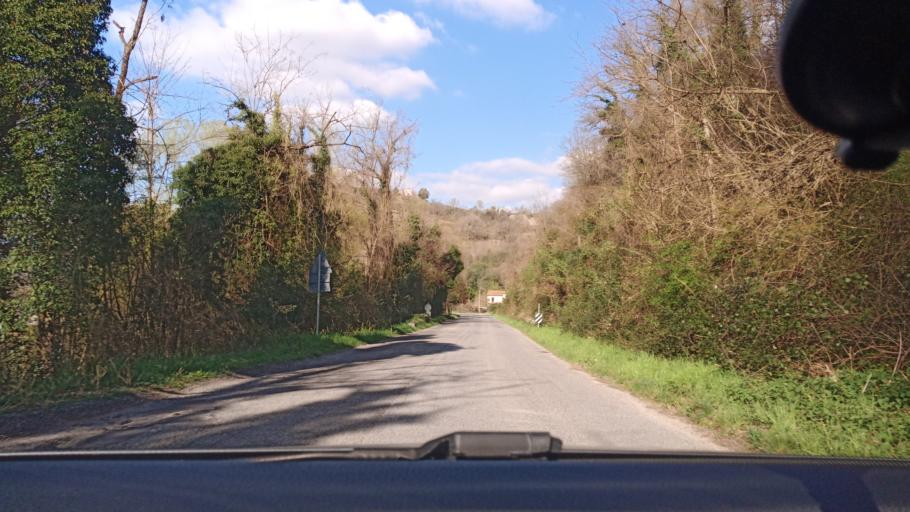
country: IT
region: Latium
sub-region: Citta metropolitana di Roma Capitale
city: Torrita Tiberina
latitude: 42.2367
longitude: 12.6328
